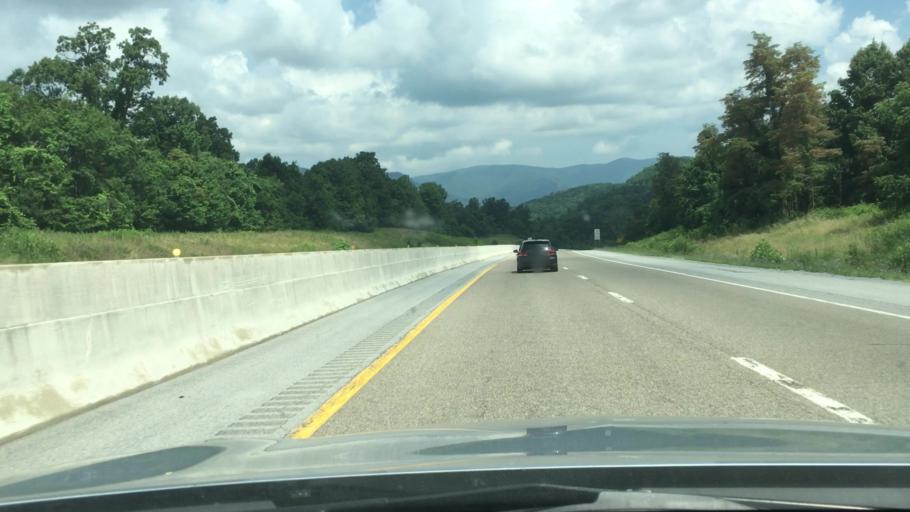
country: US
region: North Carolina
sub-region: Madison County
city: Mars Hill
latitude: 35.9883
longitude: -82.5432
